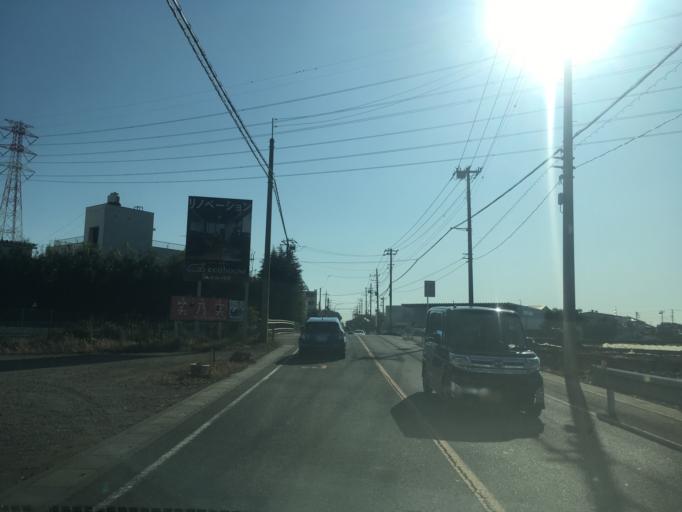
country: JP
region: Saitama
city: Kawagoe
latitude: 35.8784
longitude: 139.4749
